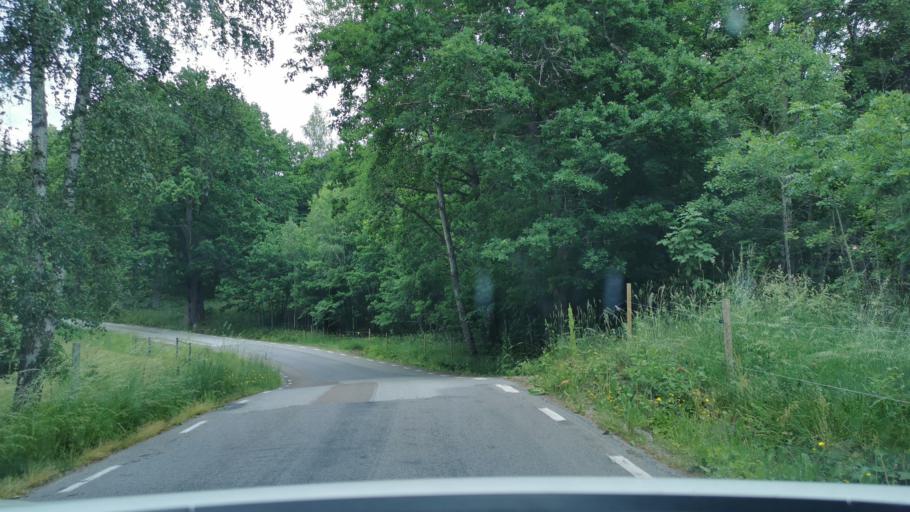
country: SE
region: Vaestra Goetaland
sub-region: Bengtsfors Kommun
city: Dals Langed
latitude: 58.8448
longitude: 12.4090
